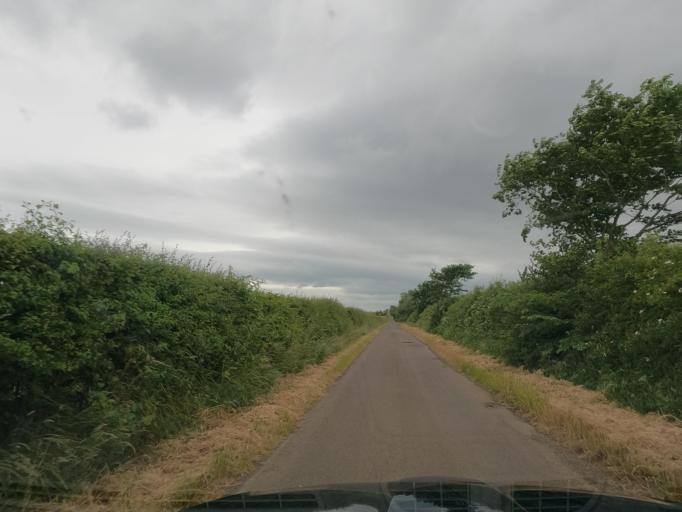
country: GB
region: England
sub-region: Northumberland
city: Ford
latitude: 55.6721
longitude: -2.0497
